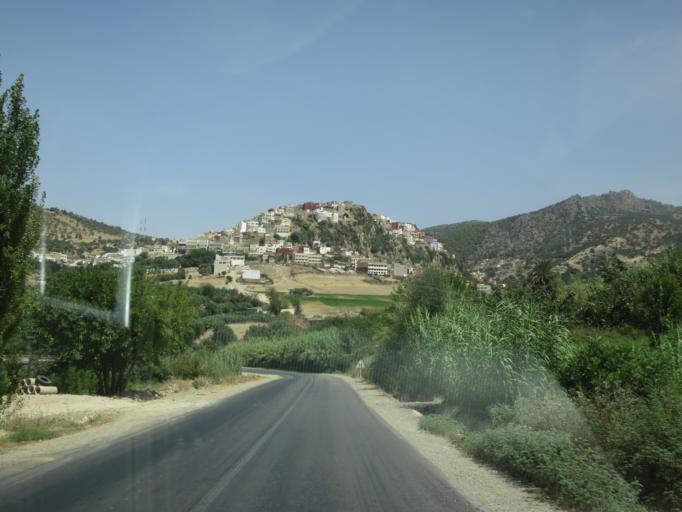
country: MA
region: Meknes-Tafilalet
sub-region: Meknes
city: Meknes
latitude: 34.0525
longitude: -5.5342
